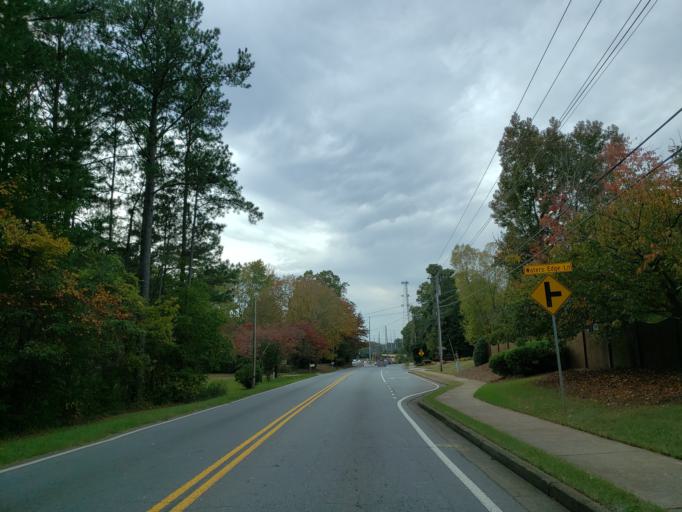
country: US
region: Georgia
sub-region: Cobb County
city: Kennesaw
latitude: 34.0659
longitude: -84.6216
